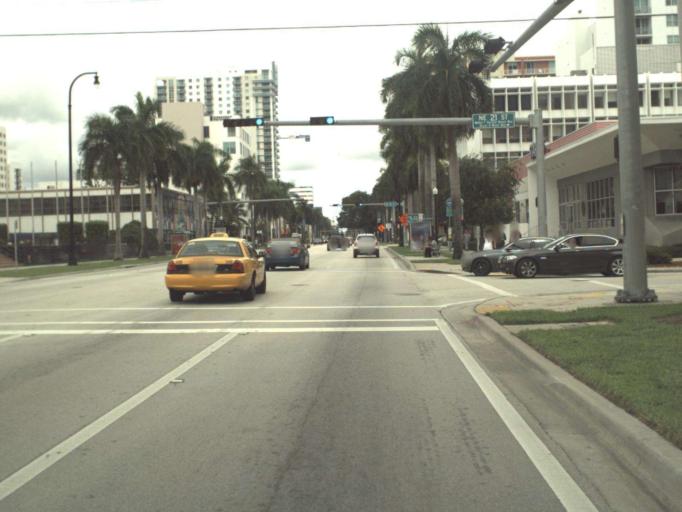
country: US
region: Florida
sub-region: Miami-Dade County
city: Miami
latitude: 25.7969
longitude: -80.1890
